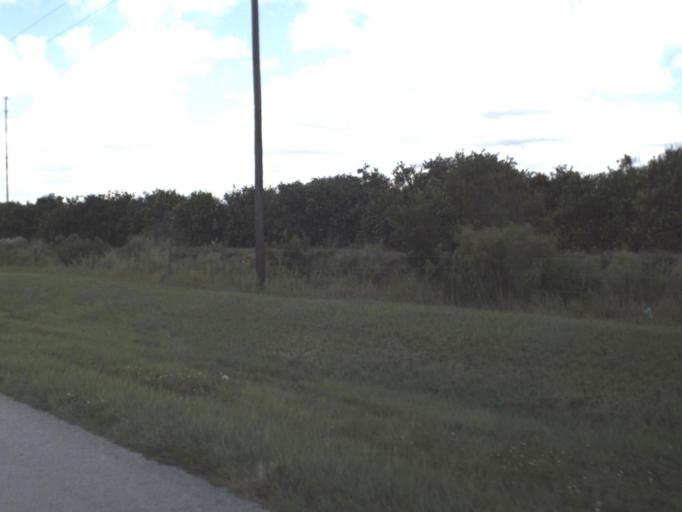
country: US
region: Florida
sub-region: Highlands County
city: Sebring
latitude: 27.4214
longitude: -81.5736
